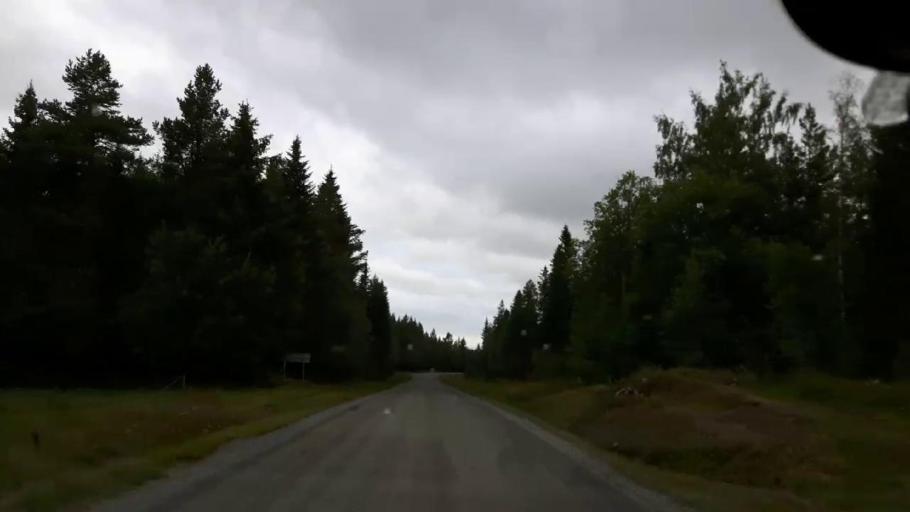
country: SE
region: Jaemtland
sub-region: OEstersunds Kommun
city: Ostersund
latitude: 63.0598
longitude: 14.5556
